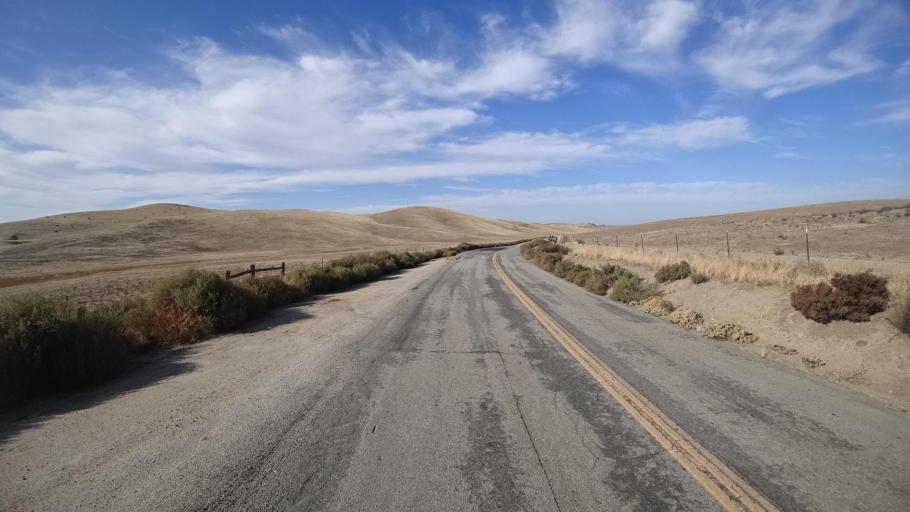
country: US
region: California
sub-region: Kern County
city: Oildale
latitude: 35.6054
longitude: -118.9517
